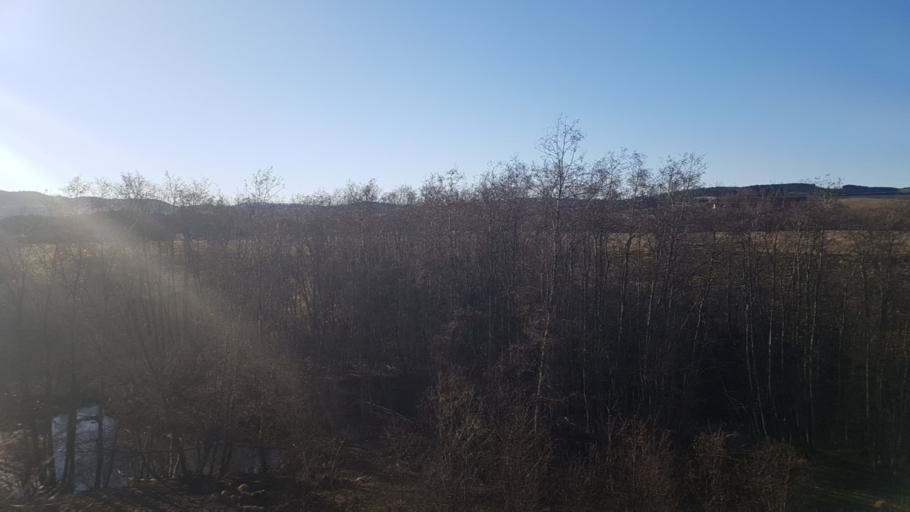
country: NO
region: Nord-Trondelag
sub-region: Levanger
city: Skogn
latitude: 63.6960
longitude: 11.1814
